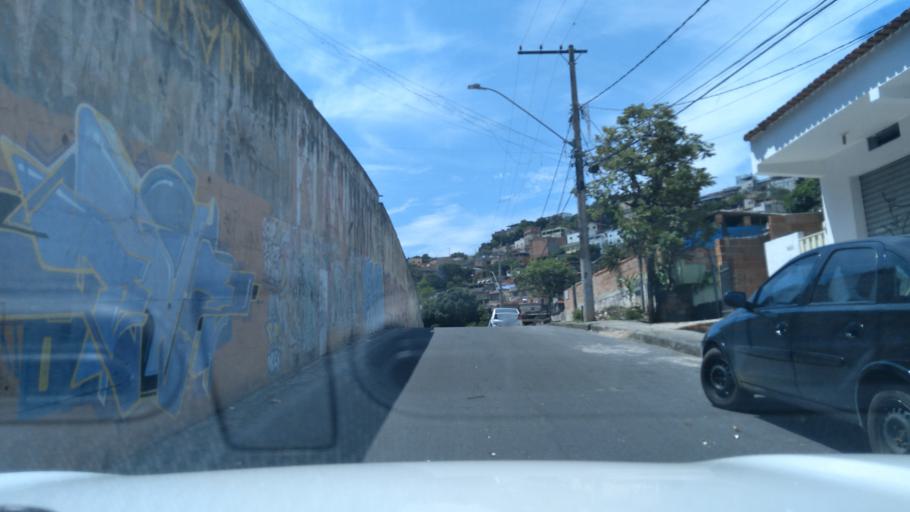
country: BR
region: Minas Gerais
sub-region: Contagem
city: Contagem
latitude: -19.9154
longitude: -44.0227
